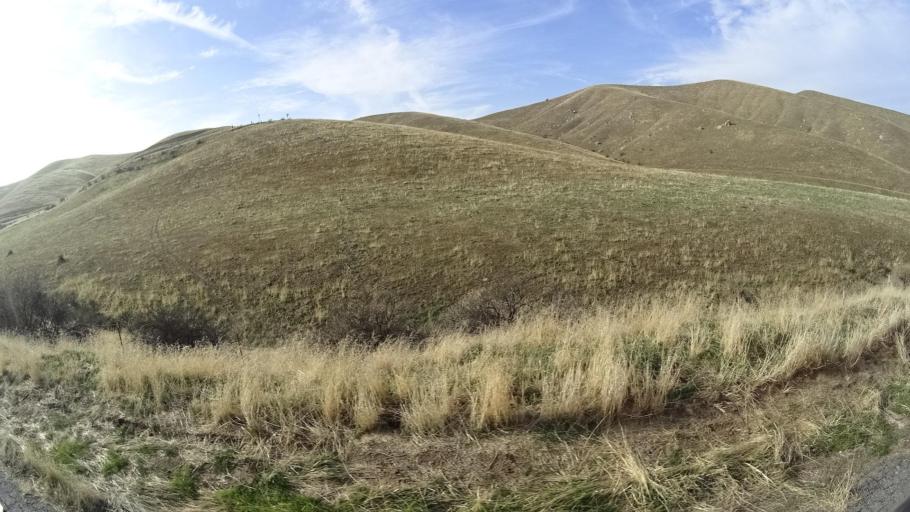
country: US
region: California
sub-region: Kern County
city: Bear Valley Springs
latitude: 35.2822
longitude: -118.6732
